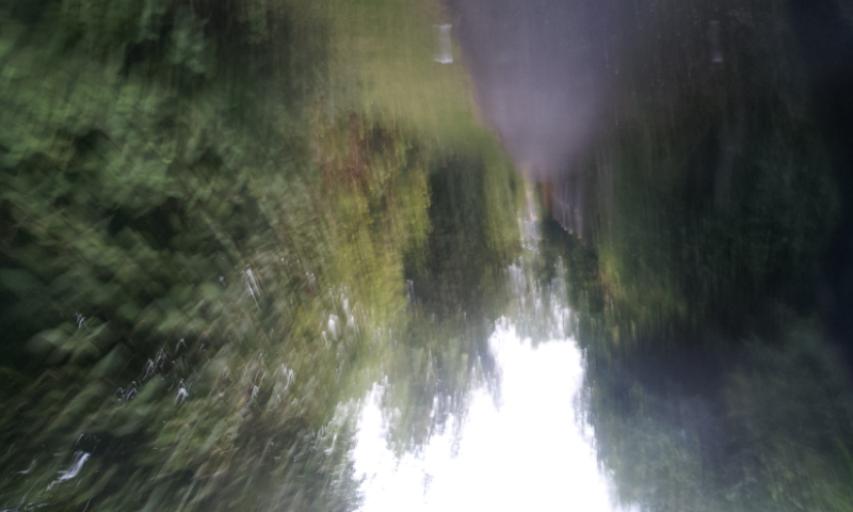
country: GB
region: England
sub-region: Kent
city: Chatham
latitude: 51.3638
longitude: 0.5478
